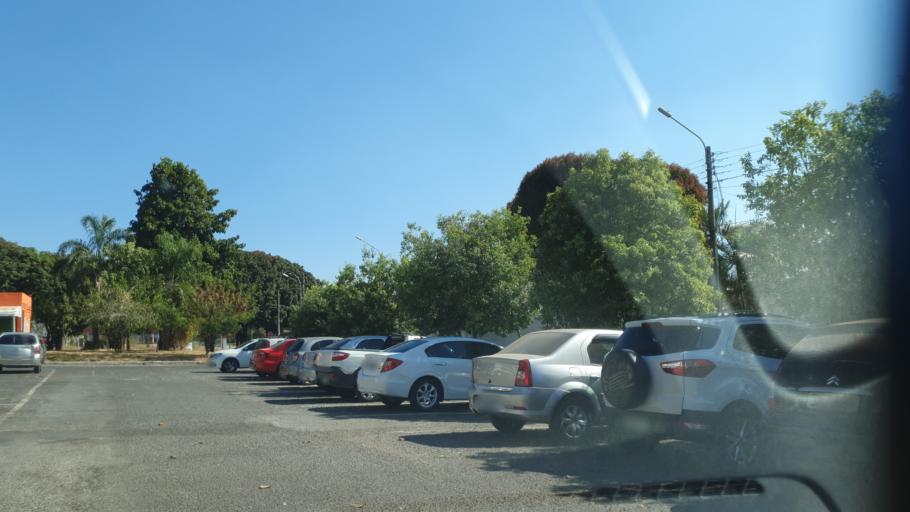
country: BR
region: Federal District
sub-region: Brasilia
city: Brasilia
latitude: -15.7895
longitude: -47.9352
